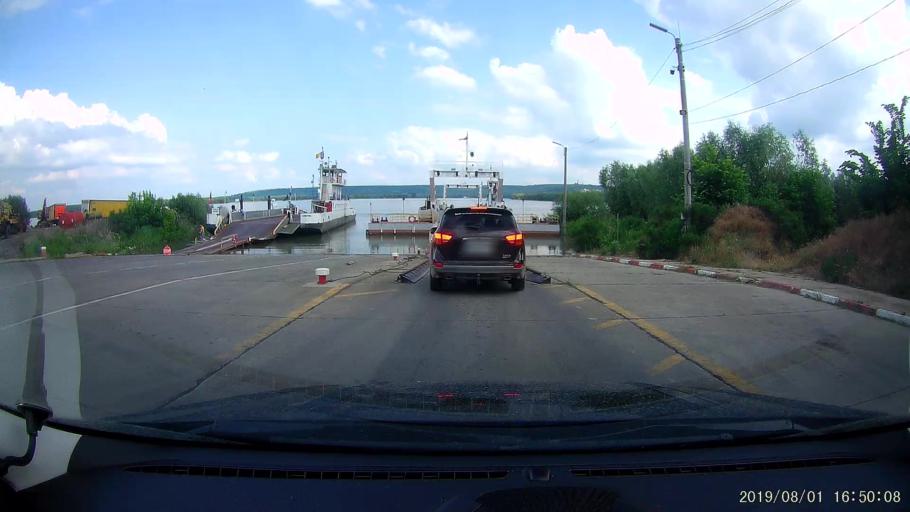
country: BG
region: Silistra
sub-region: Obshtina Silistra
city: Silistra
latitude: 44.1317
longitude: 27.2680
